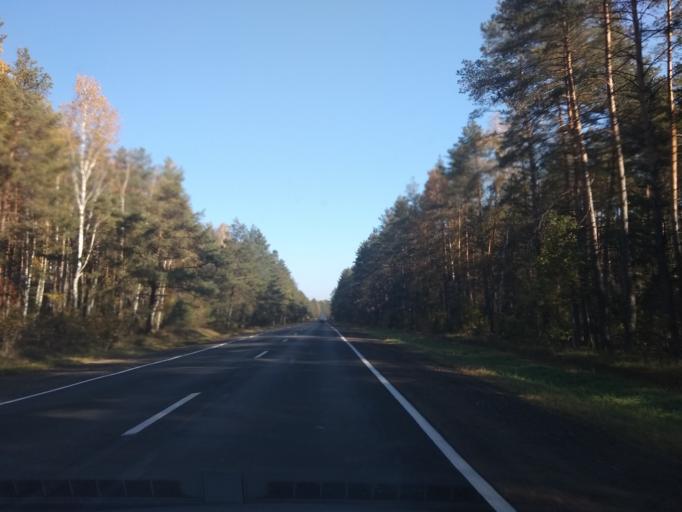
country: BY
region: Brest
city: Baranovichi
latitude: 53.0432
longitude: 25.8180
